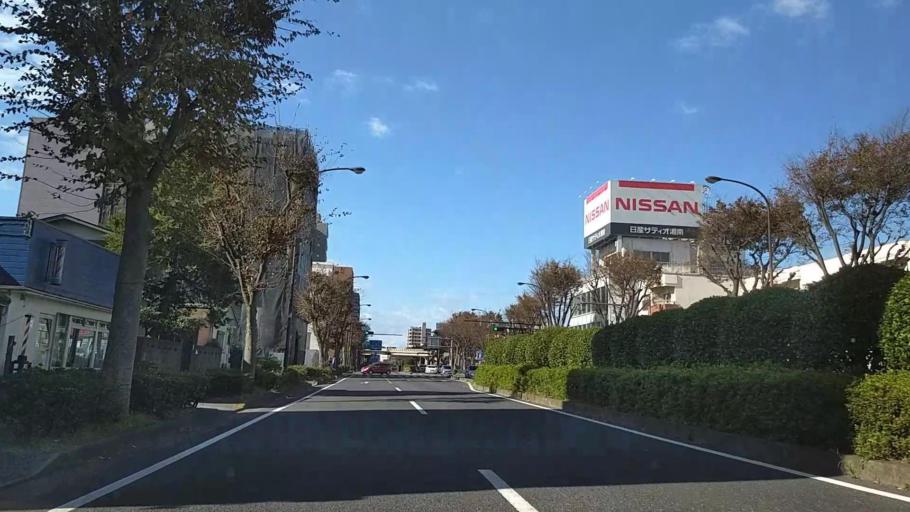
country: JP
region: Kanagawa
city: Hiratsuka
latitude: 35.3328
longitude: 139.3523
